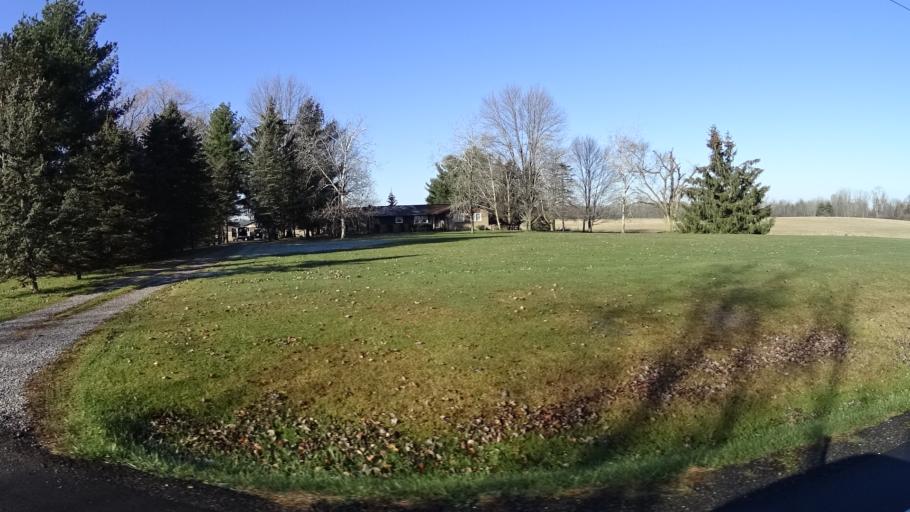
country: US
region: Ohio
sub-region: Lorain County
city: Lagrange
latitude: 41.1566
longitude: -82.1221
